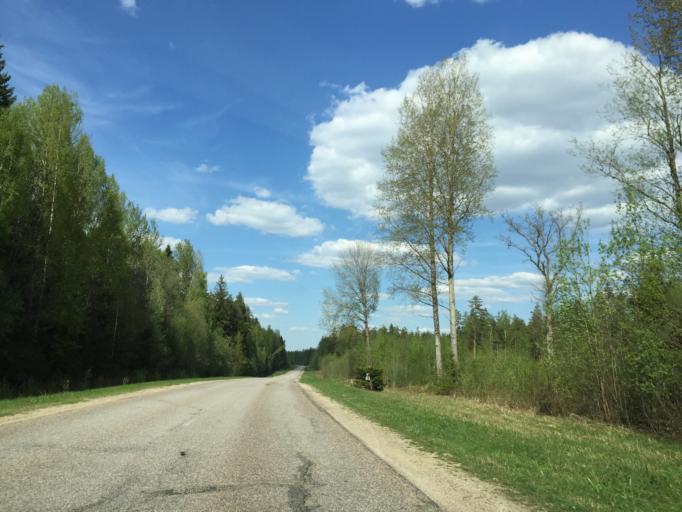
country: LV
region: Limbazu Rajons
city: Limbazi
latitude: 57.4155
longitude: 24.6983
